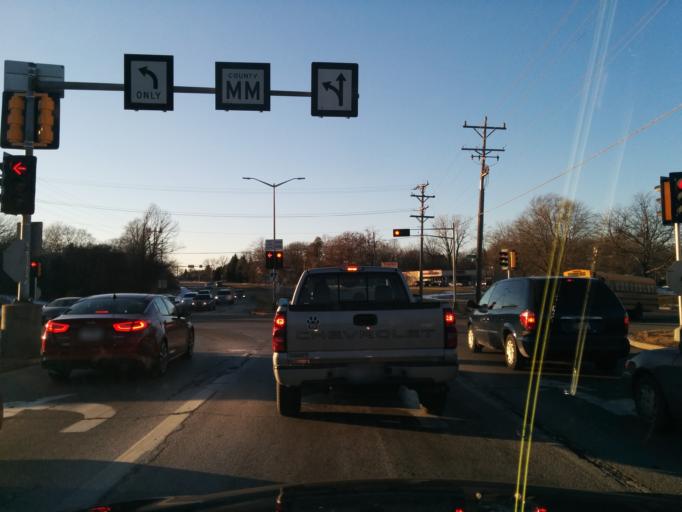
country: US
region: Wisconsin
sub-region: Racine County
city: Racine
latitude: 42.7519
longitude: -87.8243
